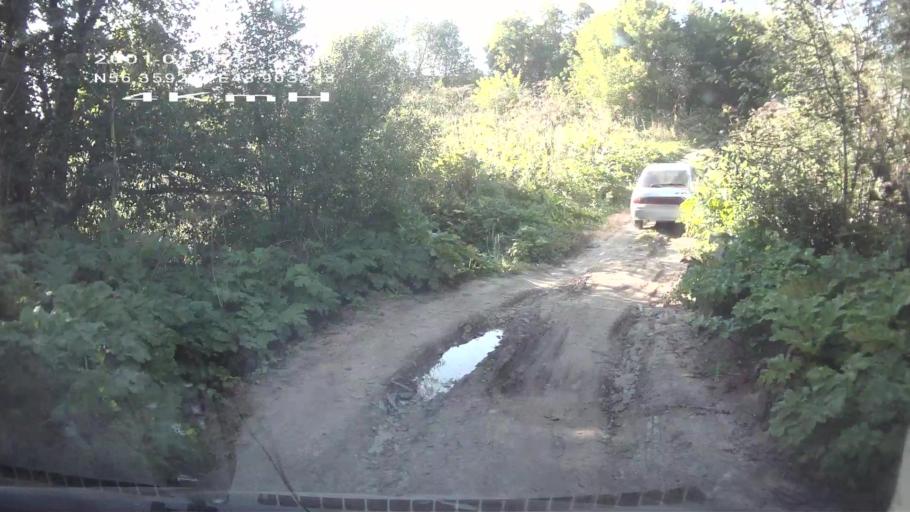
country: RU
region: Mariy-El
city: Morki
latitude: 56.3593
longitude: 48.9031
